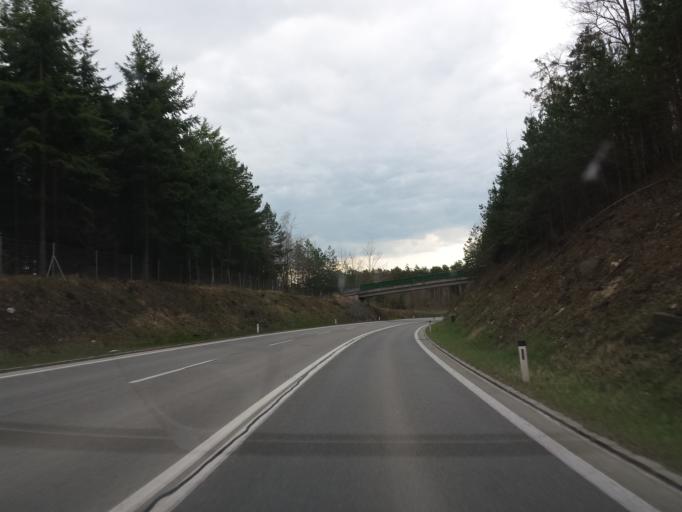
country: AT
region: Lower Austria
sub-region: Politischer Bezirk Krems
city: Lengenfeld
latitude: 48.4887
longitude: 15.5808
